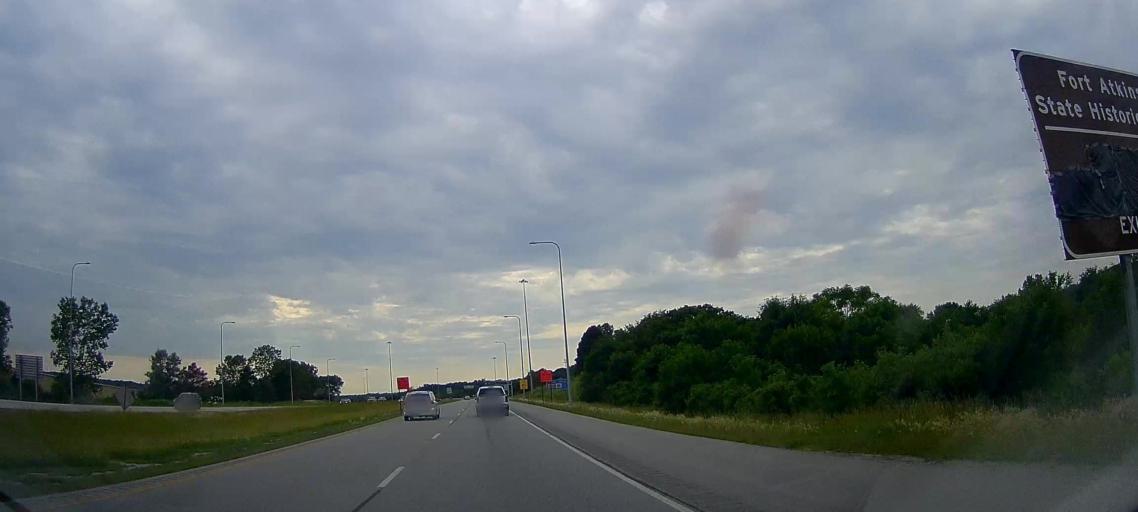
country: US
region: Iowa
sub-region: Pottawattamie County
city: Carter Lake
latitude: 41.3461
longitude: -95.9747
